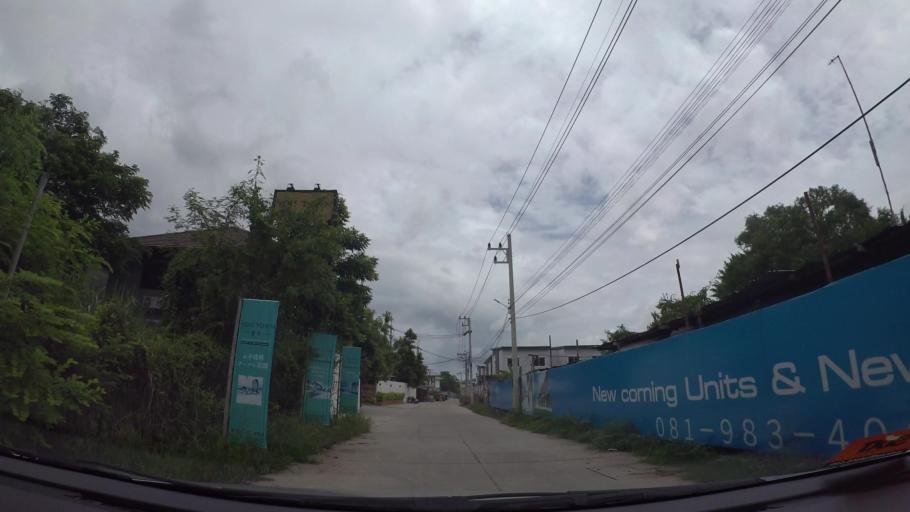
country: TH
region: Chon Buri
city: Si Racha
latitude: 13.1590
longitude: 100.9792
